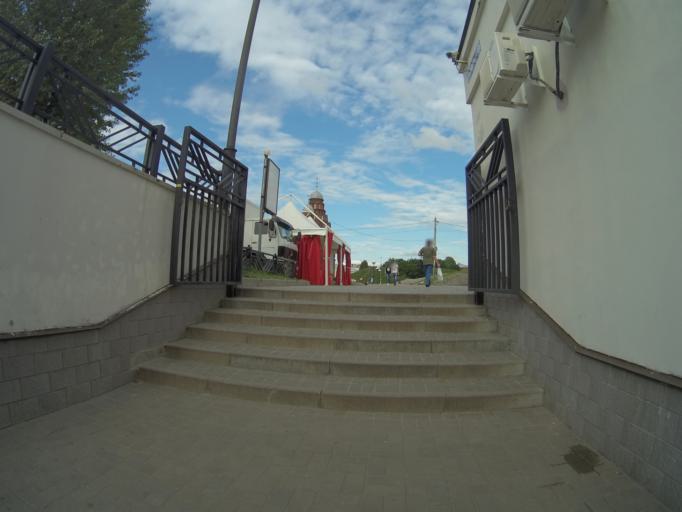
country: RU
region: Vladimir
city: Vladimir
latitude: 56.1260
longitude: 40.3942
